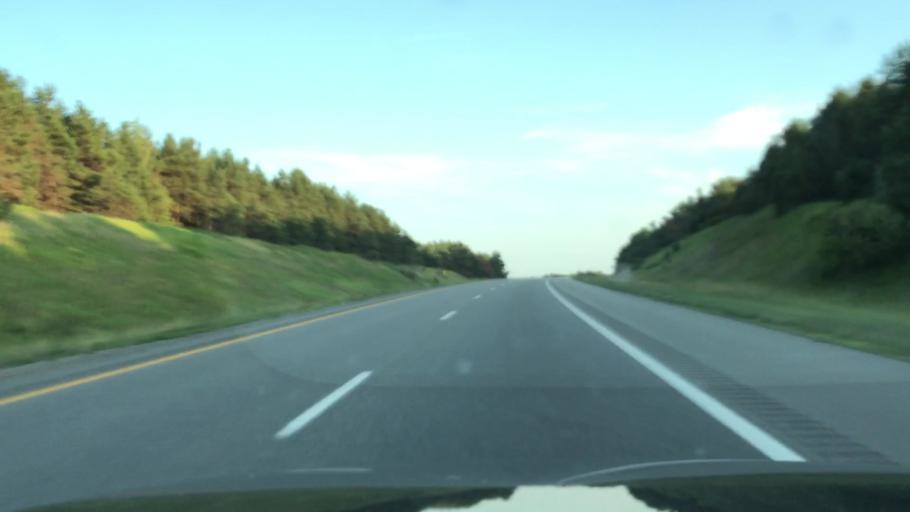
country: US
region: Michigan
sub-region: Osceola County
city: Reed City
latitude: 43.8515
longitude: -85.5327
